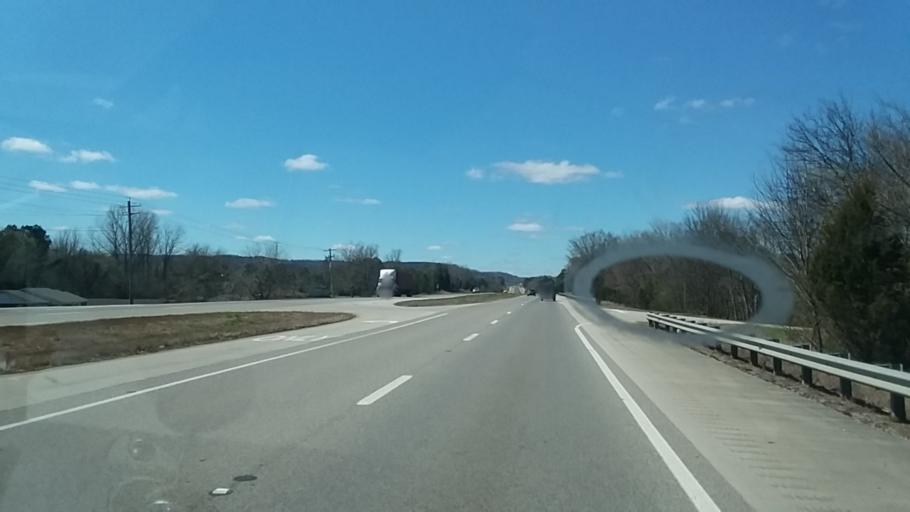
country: US
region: Alabama
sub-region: Colbert County
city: Cherokee
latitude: 34.7319
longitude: -87.8640
